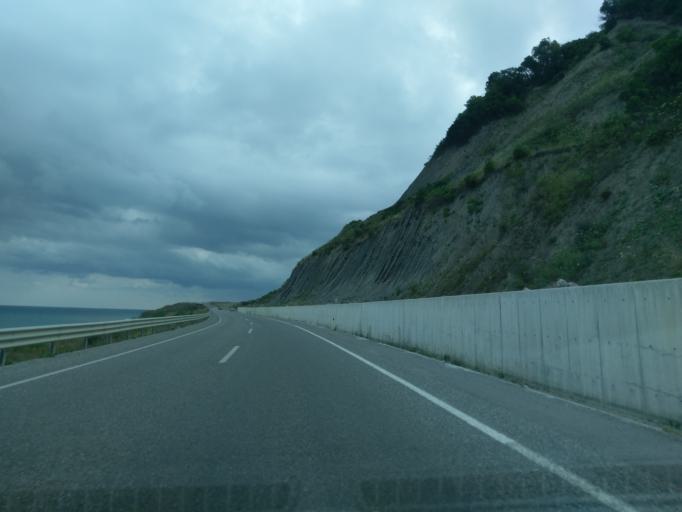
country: TR
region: Sinop
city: Helaldi
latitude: 41.9484
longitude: 34.3695
